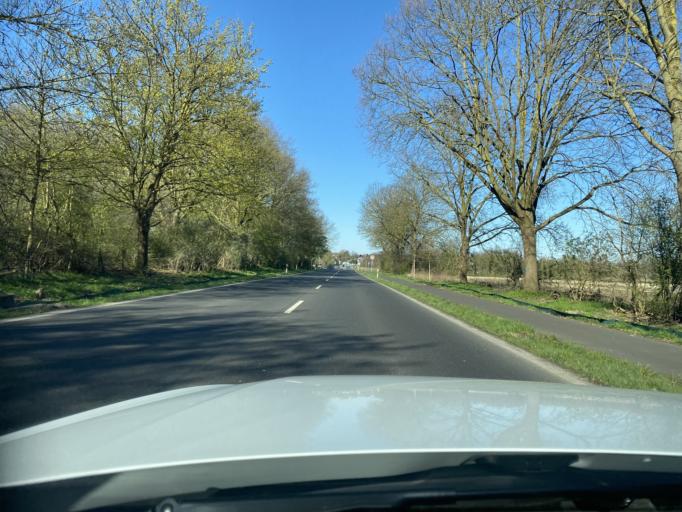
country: DE
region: North Rhine-Westphalia
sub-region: Regierungsbezirk Dusseldorf
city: Grevenbroich
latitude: 51.1015
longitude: 6.5978
